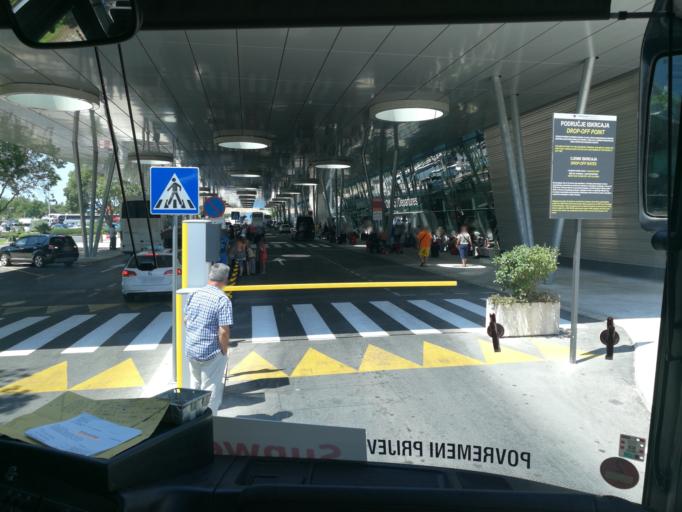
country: HR
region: Dubrovacko-Neretvanska
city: Jasenice
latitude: 42.5597
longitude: 18.2630
